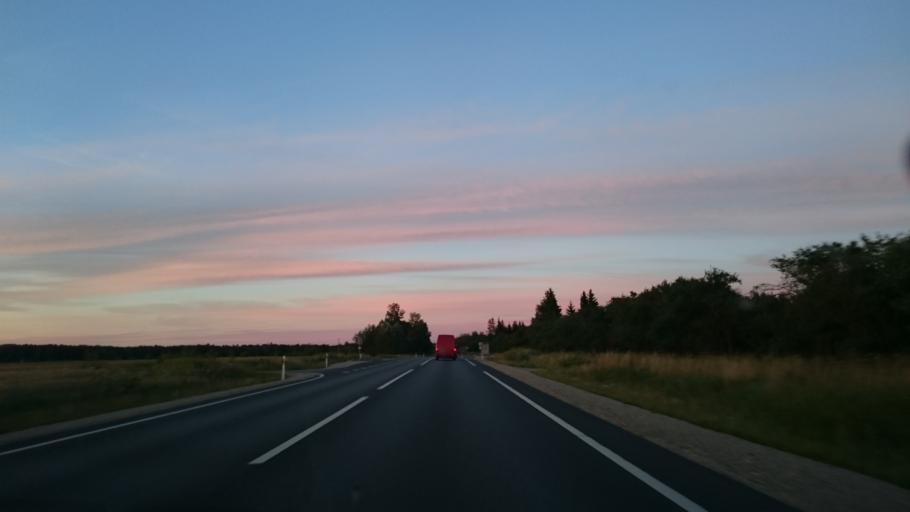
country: LV
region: Dobeles Rajons
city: Dobele
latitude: 56.7432
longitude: 23.2497
